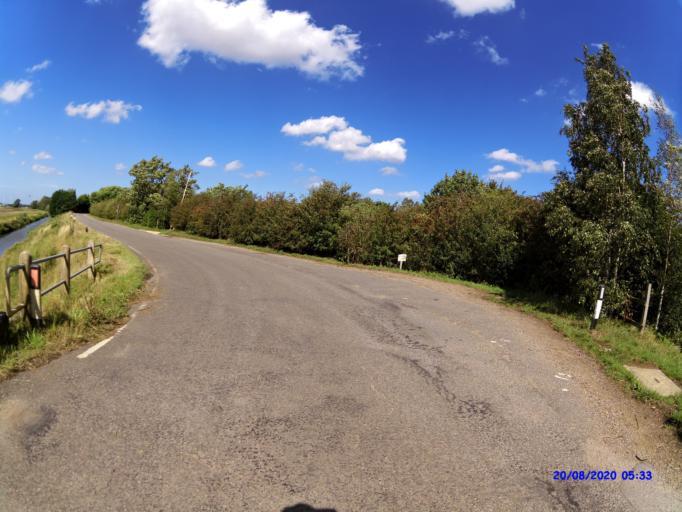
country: GB
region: England
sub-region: Cambridgeshire
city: Whittlesey
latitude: 52.5438
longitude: -0.1109
